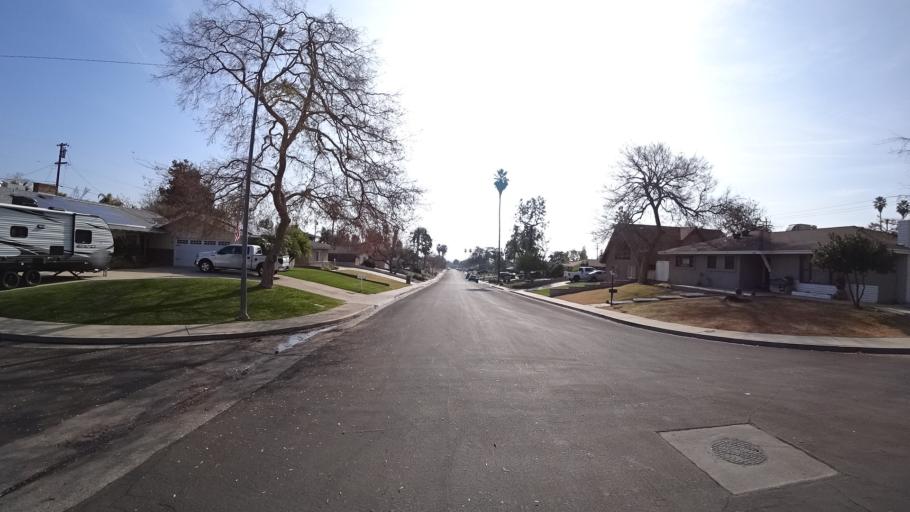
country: US
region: California
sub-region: Kern County
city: Bakersfield
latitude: 35.3881
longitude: -118.9490
